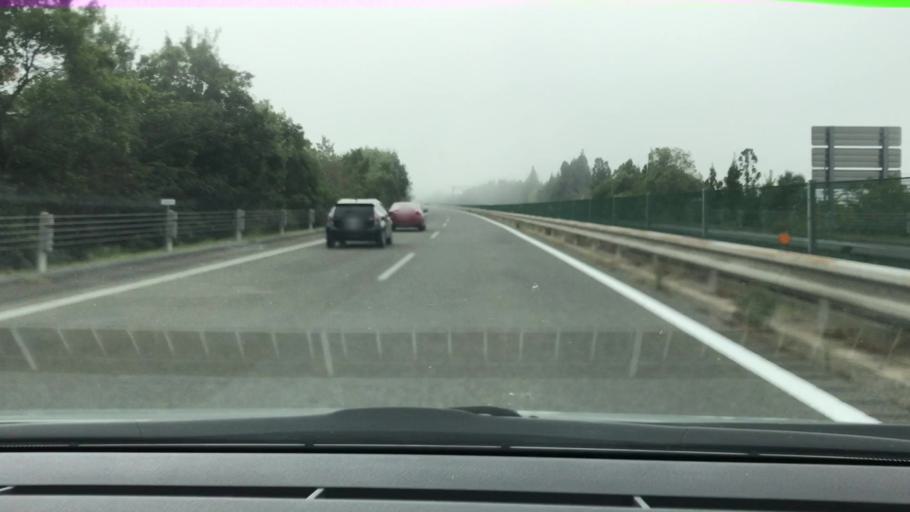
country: JP
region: Hyogo
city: Sasayama
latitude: 35.0754
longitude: 135.1708
